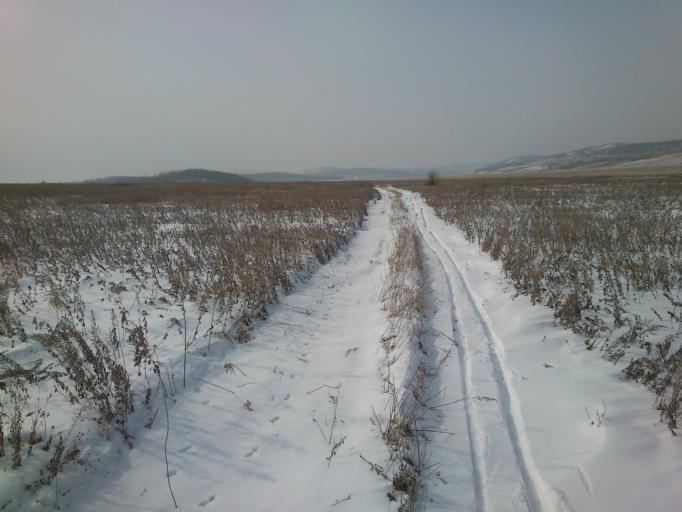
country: RU
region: Primorskiy
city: Sergeyevka
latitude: 44.3698
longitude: 131.8481
